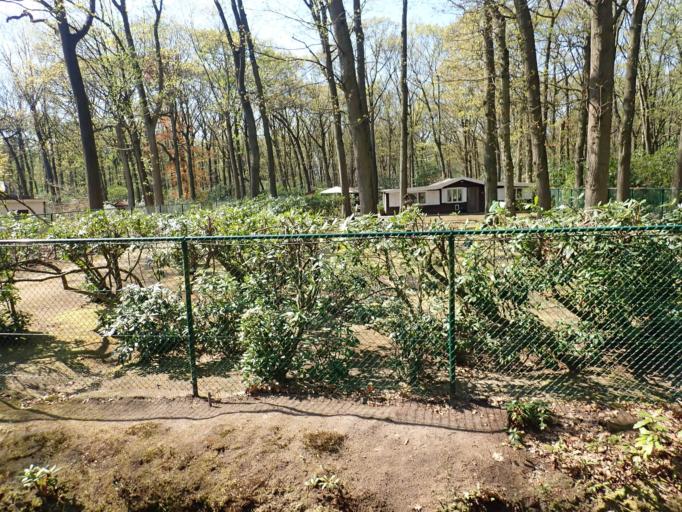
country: BE
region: Flanders
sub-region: Provincie Antwerpen
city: Brasschaat
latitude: 51.3422
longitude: 4.5251
